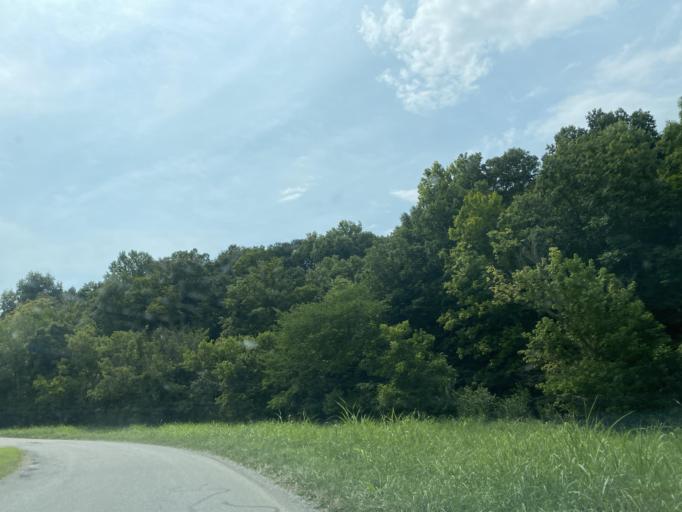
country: US
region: Kentucky
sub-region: Pendleton County
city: Falmouth
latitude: 38.7979
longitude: -84.3108
